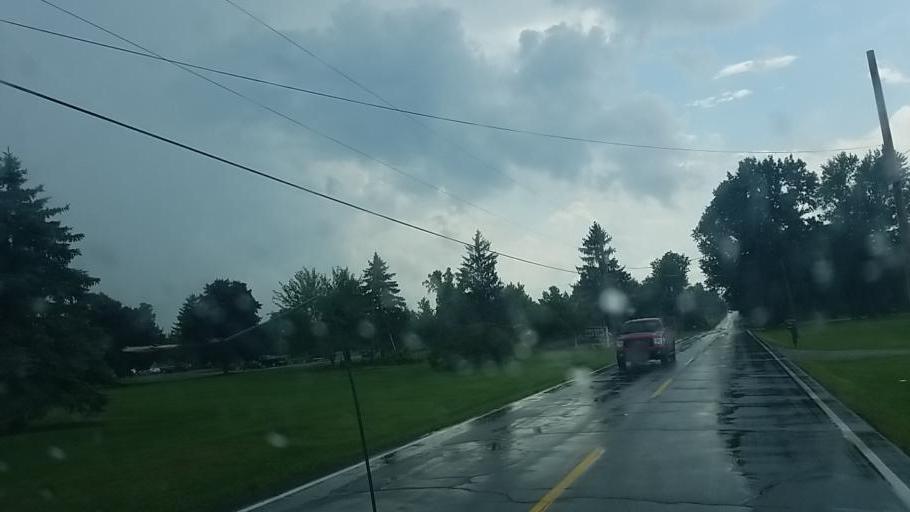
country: US
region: Ohio
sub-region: Lorain County
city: Lagrange
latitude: 41.2457
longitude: -82.0843
